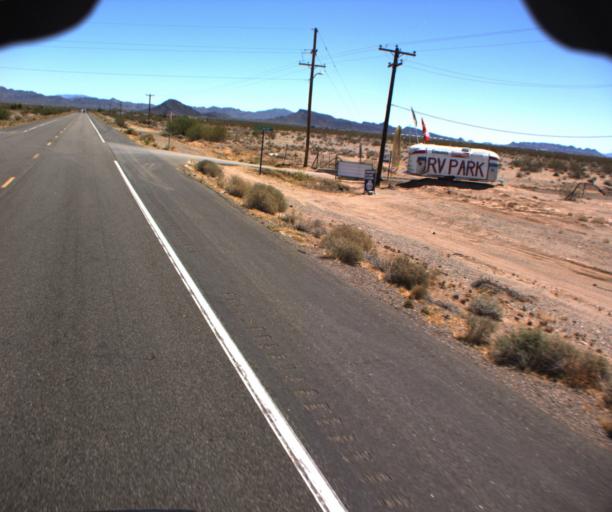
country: US
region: Arizona
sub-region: La Paz County
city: Salome
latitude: 33.7082
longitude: -113.8197
